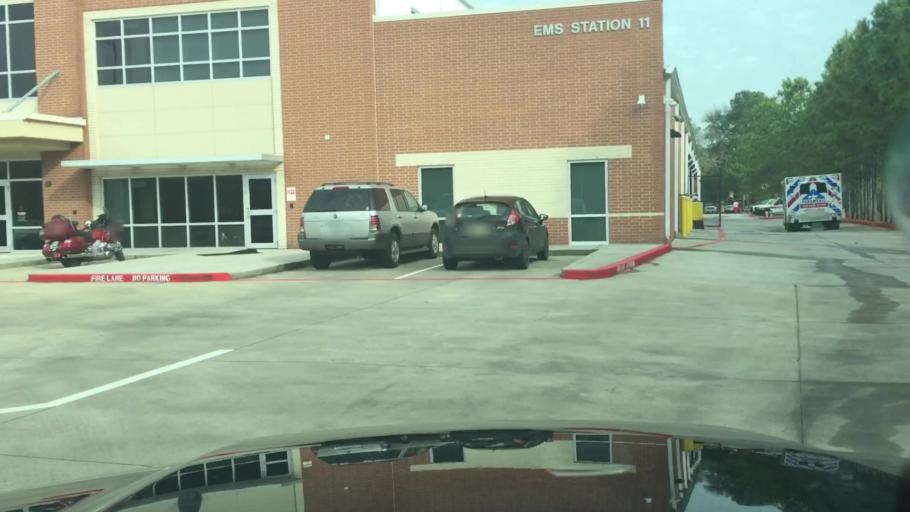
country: US
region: Texas
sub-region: Montgomery County
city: Conroe
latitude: 30.2834
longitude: -95.4767
